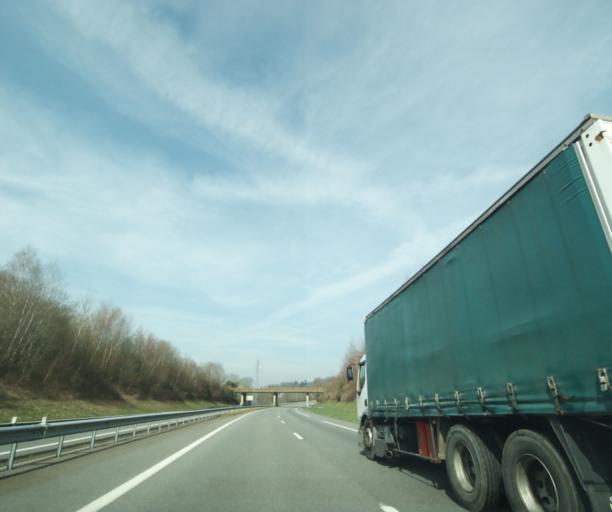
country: FR
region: Limousin
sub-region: Departement de la Correze
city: Uzerche
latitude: 45.5009
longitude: 1.5171
